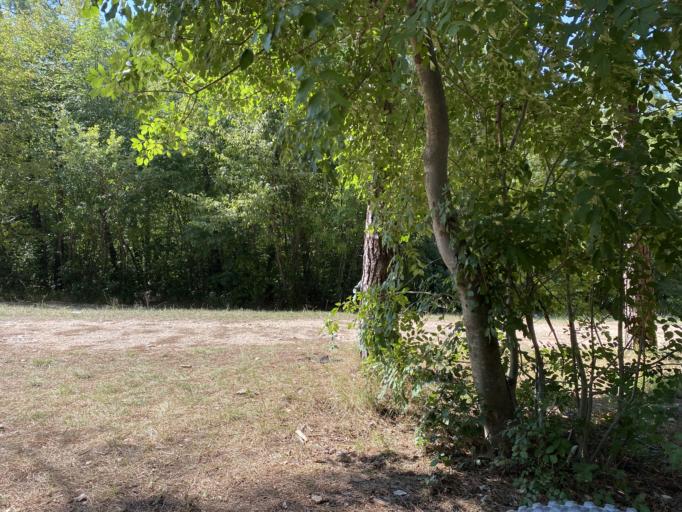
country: IT
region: The Marches
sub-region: Provincia di Ancona
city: Fabriano
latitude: 43.3152
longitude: 12.9043
